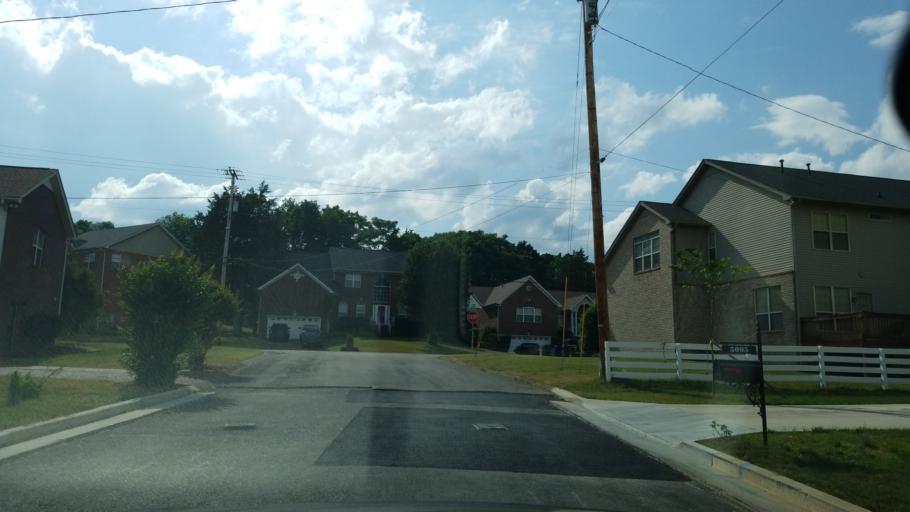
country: US
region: Tennessee
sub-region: Rutherford County
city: La Vergne
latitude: 36.0689
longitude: -86.5922
